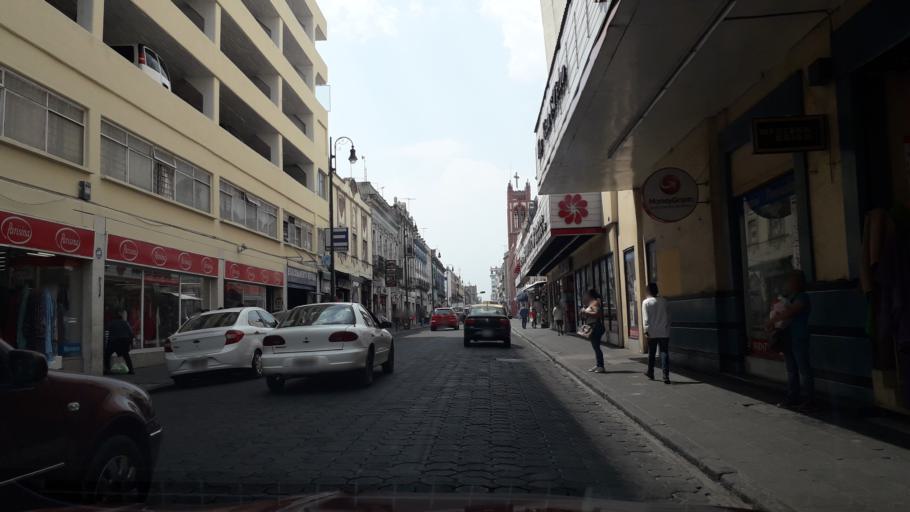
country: MX
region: Puebla
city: Puebla
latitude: 19.0461
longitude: -98.1999
